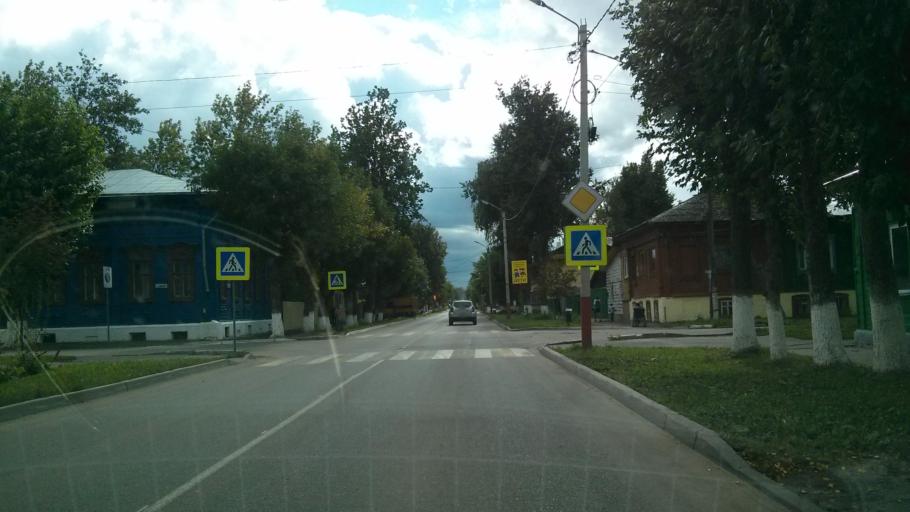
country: RU
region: Vladimir
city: Murom
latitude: 55.5730
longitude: 42.0618
